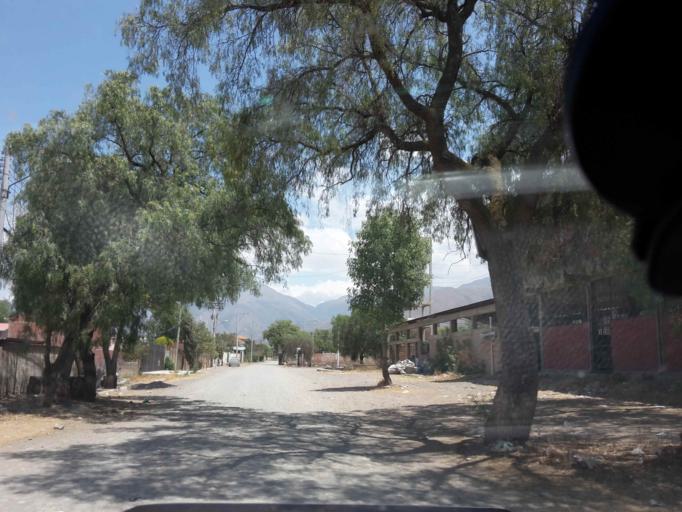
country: BO
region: Cochabamba
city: Cochabamba
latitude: -17.3363
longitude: -66.2142
